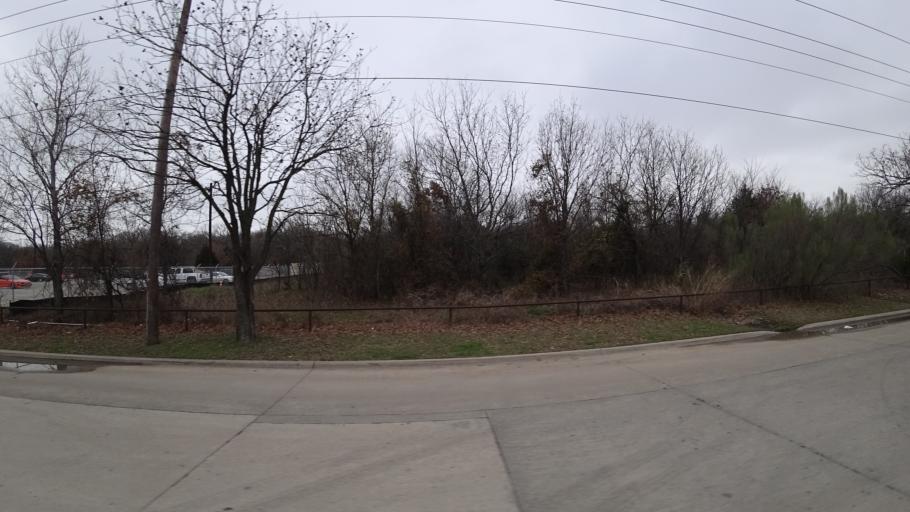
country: US
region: Texas
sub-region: Denton County
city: Lewisville
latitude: 33.0614
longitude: -96.9925
